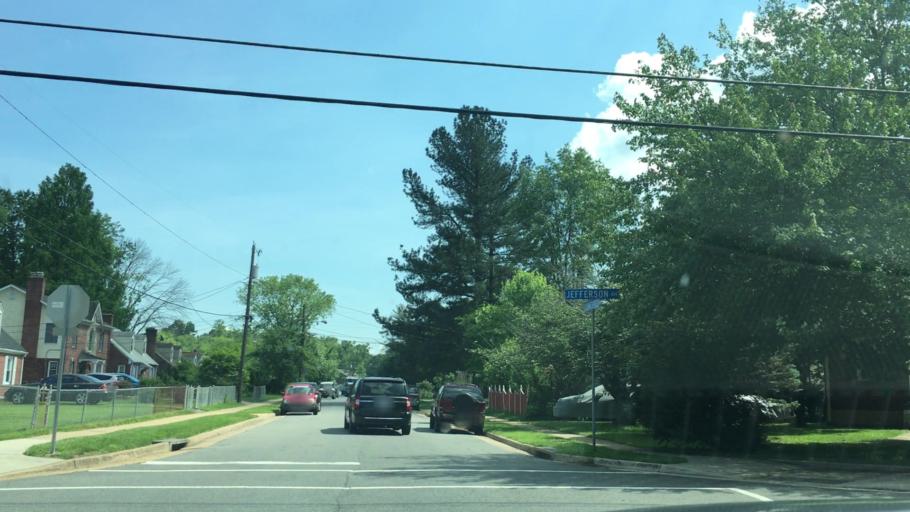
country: US
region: Virginia
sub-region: Fairfax County
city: Jefferson
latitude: 38.8708
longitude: -77.1795
